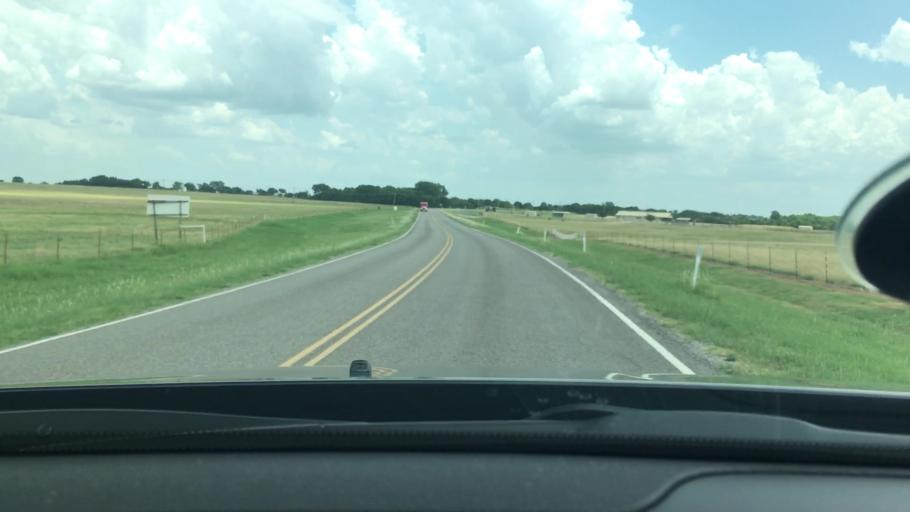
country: US
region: Oklahoma
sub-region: Love County
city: Marietta
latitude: 33.9372
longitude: -97.1055
